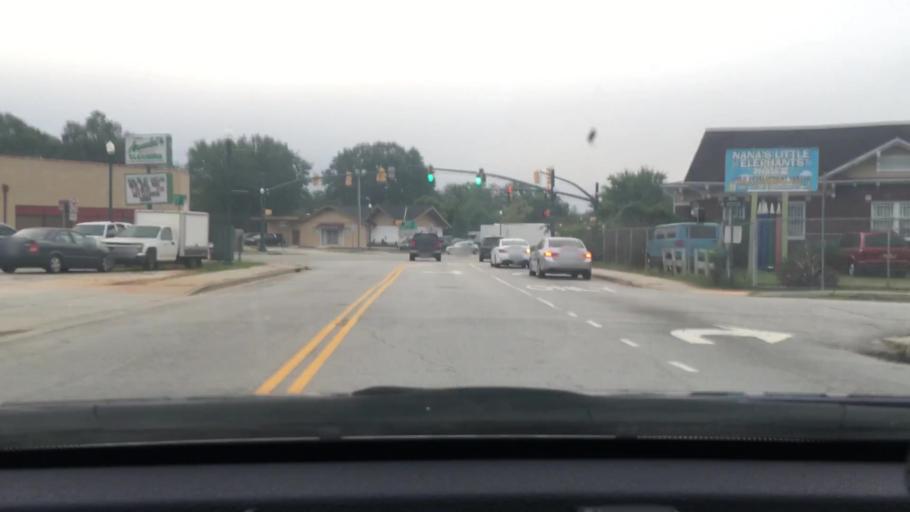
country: US
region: South Carolina
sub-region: Richland County
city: Columbia
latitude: 34.0205
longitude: -81.0426
